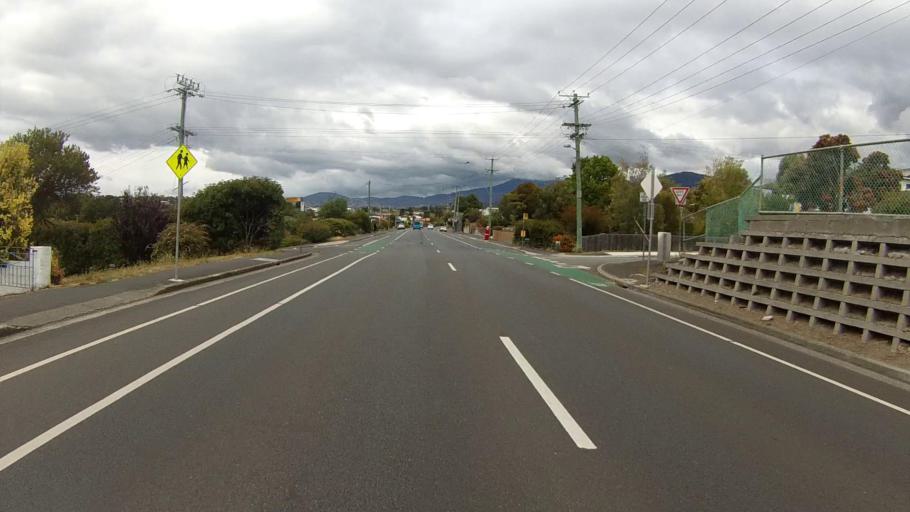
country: AU
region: Tasmania
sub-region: Glenorchy
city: Claremont
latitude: -42.7789
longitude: 147.2520
